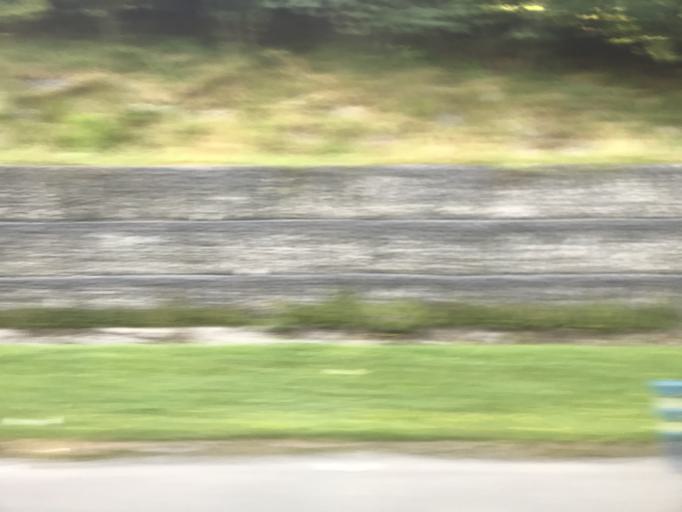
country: ES
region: Basque Country
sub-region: Provincia de Guipuzcoa
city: Anoeta
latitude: 43.1541
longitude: -2.0682
